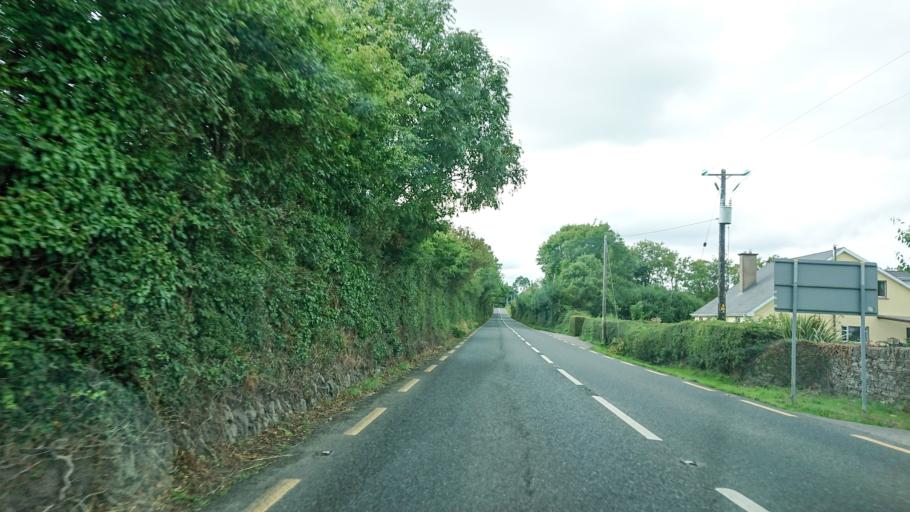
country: IE
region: Munster
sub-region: Waterford
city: Dungarvan
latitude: 52.1126
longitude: -7.5980
